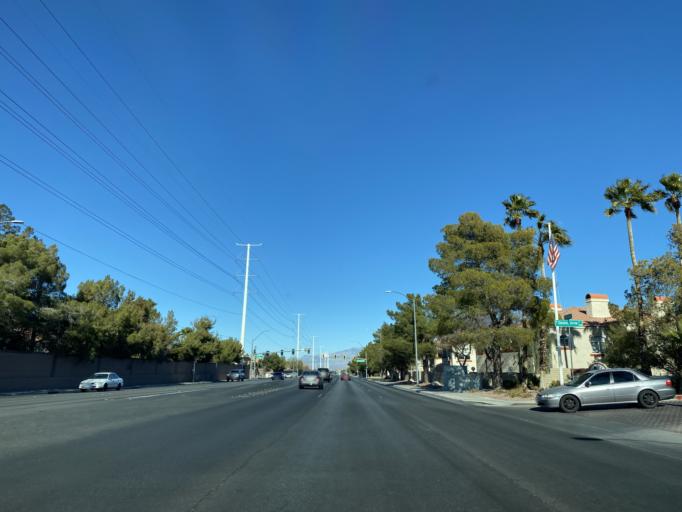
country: US
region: Nevada
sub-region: Clark County
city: Spring Valley
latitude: 36.1649
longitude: -115.2779
